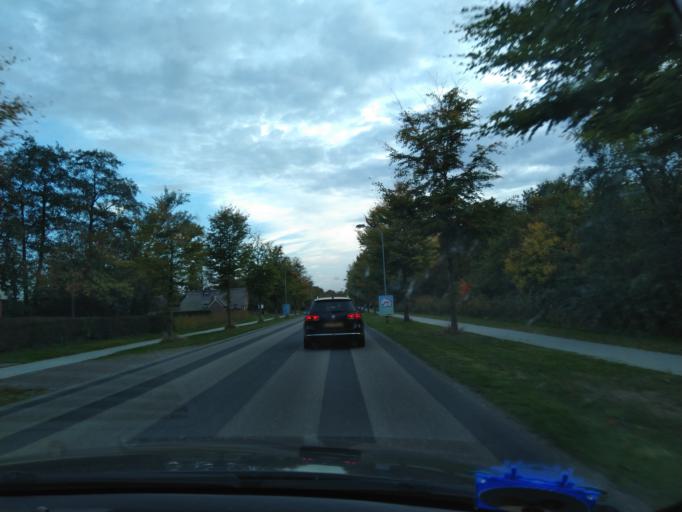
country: NL
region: Drenthe
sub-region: Gemeente Tynaarlo
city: Vries
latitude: 53.0667
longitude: 6.5772
